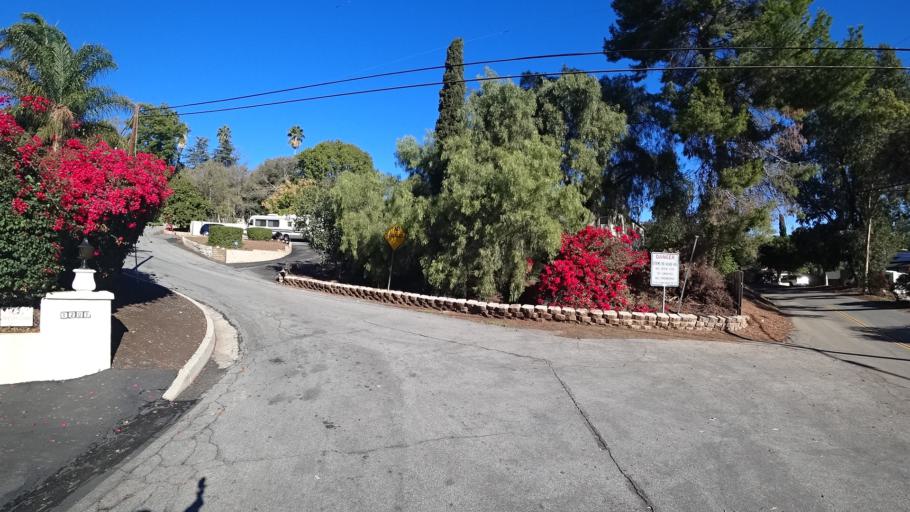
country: US
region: California
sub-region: Orange County
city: La Habra
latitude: 33.9463
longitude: -117.9419
